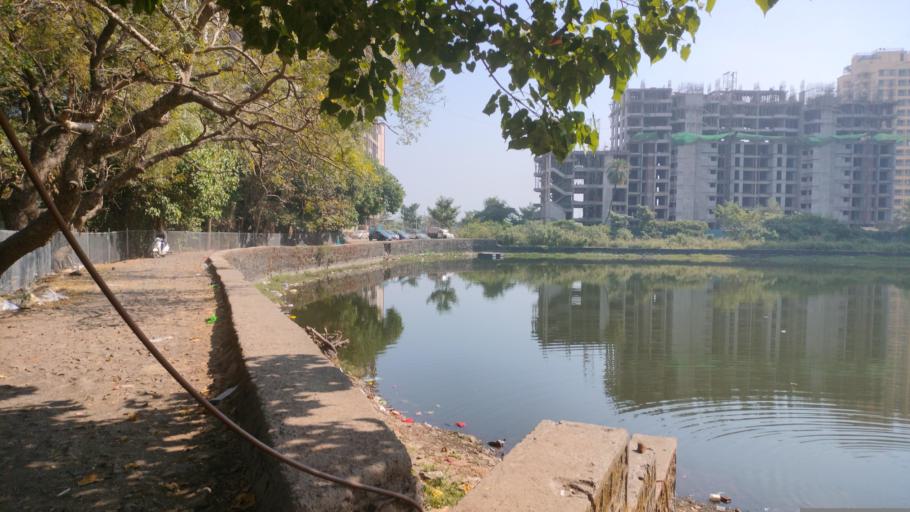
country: IN
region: Maharashtra
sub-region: Thane
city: Thane
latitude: 19.2718
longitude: 72.9697
